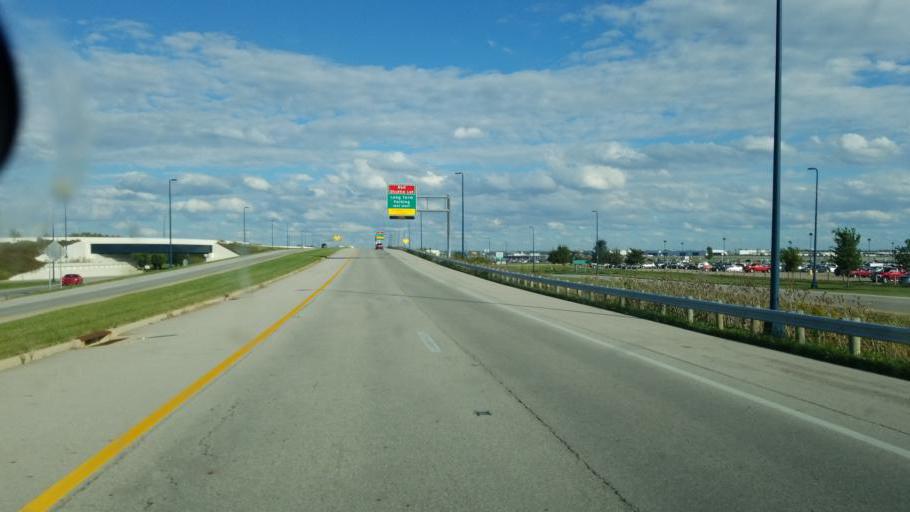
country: US
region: Ohio
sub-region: Franklin County
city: Bexley
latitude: 39.9998
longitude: -82.9170
